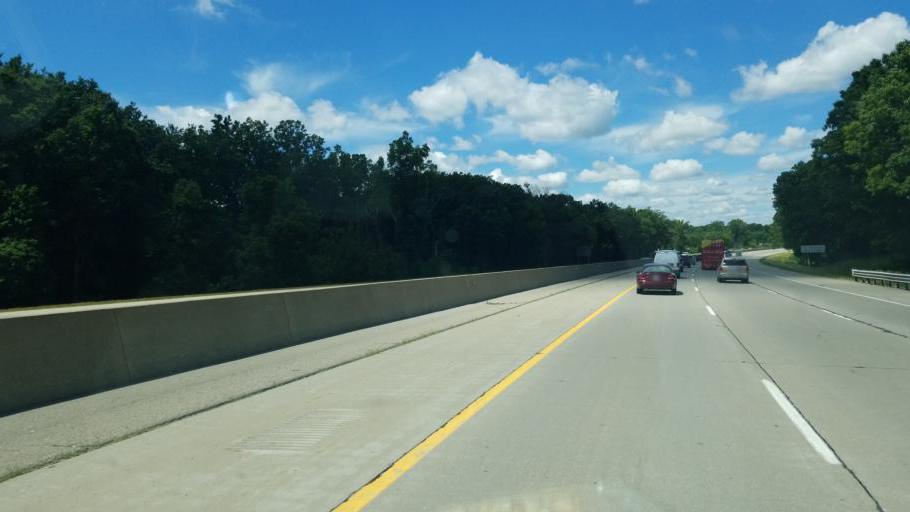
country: US
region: Michigan
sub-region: Livingston County
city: Brighton
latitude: 42.5513
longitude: -83.8036
